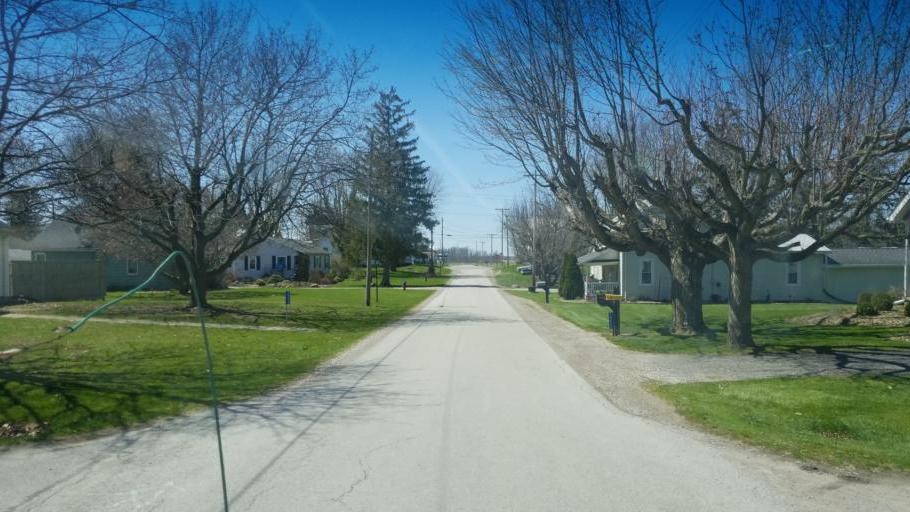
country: US
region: Ohio
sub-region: Huron County
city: Willard
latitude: 41.0518
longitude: -82.8921
